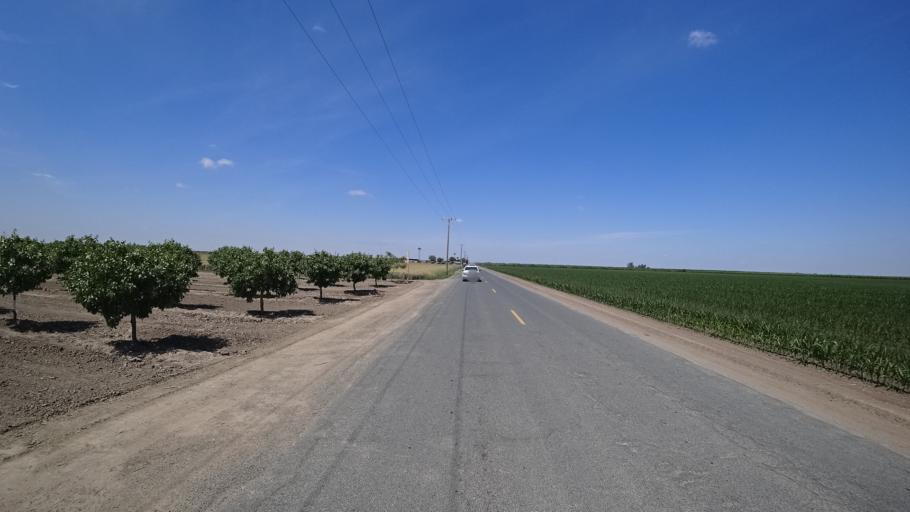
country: US
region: California
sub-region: Tulare County
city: Goshen
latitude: 36.2690
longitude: -119.4943
